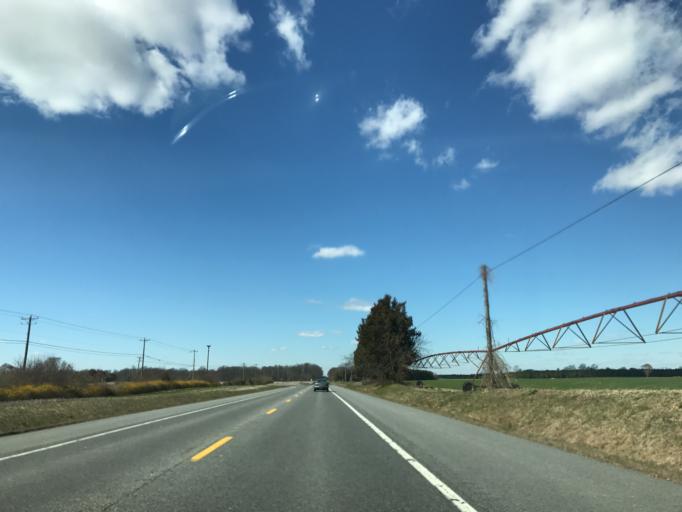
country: US
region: Maryland
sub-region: Queen Anne's County
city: Kingstown
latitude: 39.1722
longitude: -75.9908
